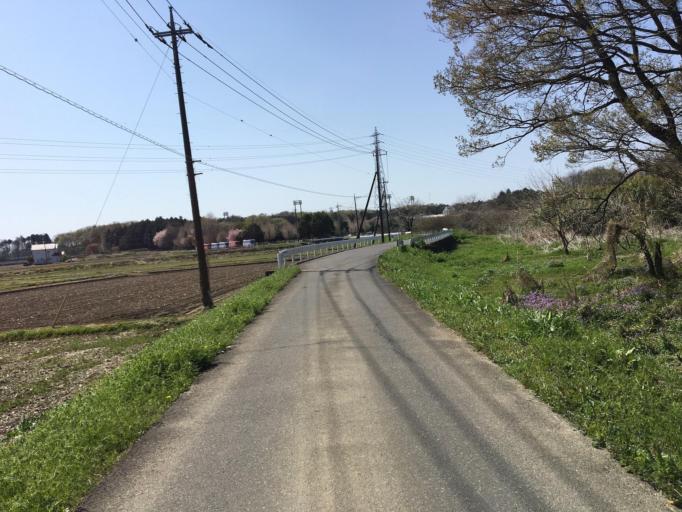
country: JP
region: Saitama
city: Sakado
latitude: 35.9625
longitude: 139.3445
